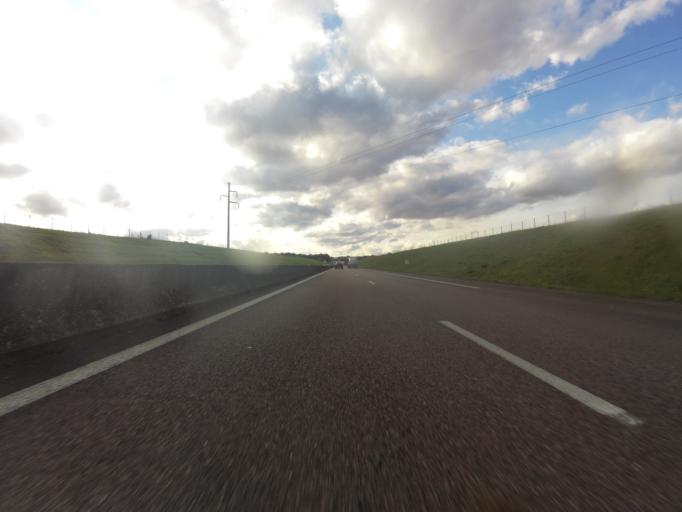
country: FR
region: Picardie
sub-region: Departement de la Somme
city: Hornoy-le-Bourg
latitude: 49.8150
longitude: 1.9261
